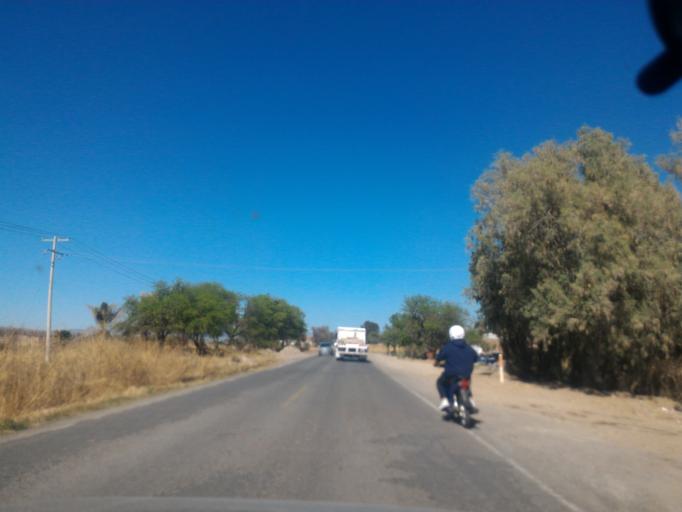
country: MX
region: Guanajuato
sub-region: Leon
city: Malagana (San Antonio del Monte)
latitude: 21.0354
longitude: -101.7732
